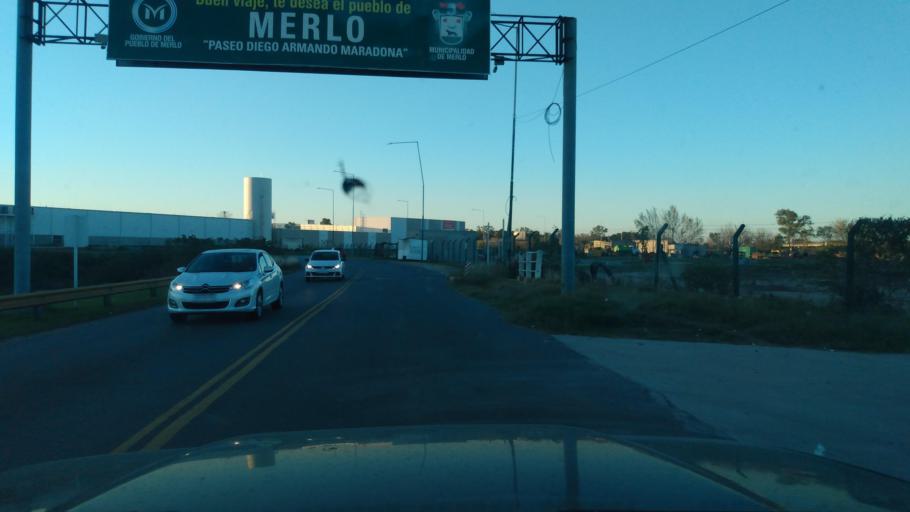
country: AR
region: Buenos Aires
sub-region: Partido de Merlo
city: Merlo
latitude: -34.6327
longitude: -58.7266
